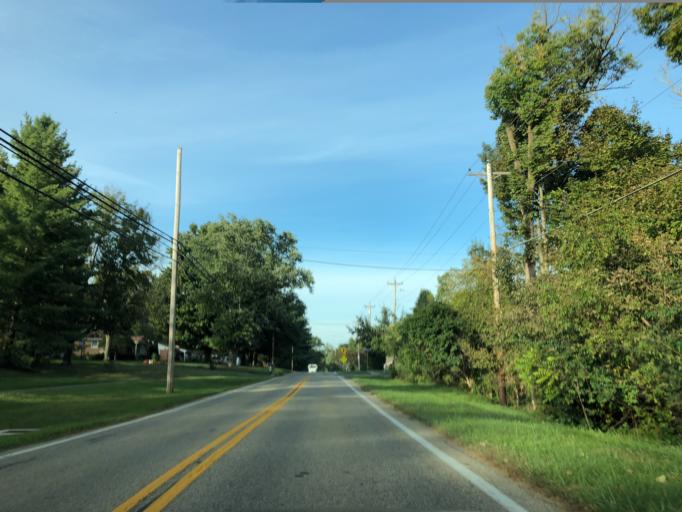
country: US
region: Ohio
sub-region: Warren County
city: Loveland Park
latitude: 39.2845
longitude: -84.2702
